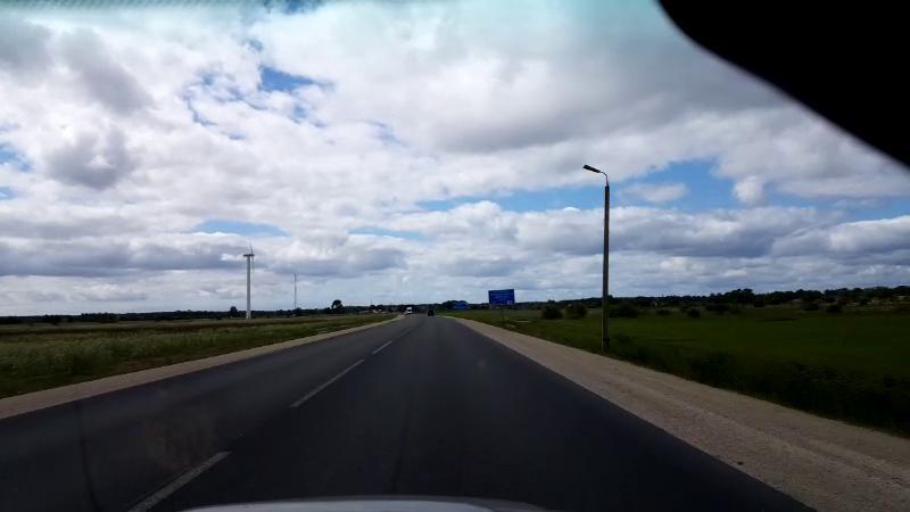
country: LV
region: Salacgrivas
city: Ainazi
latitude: 57.8685
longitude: 24.3745
